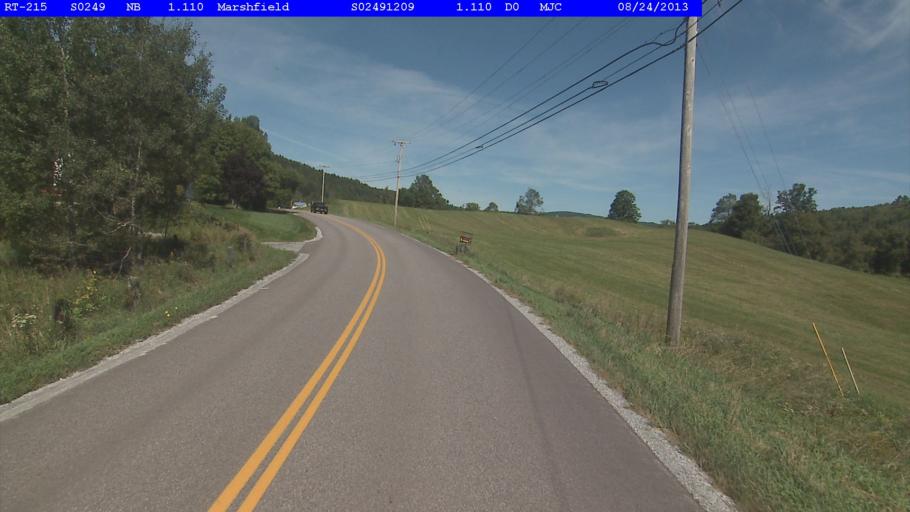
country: US
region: Vermont
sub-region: Caledonia County
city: Hardwick
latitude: 44.3636
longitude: -72.3363
